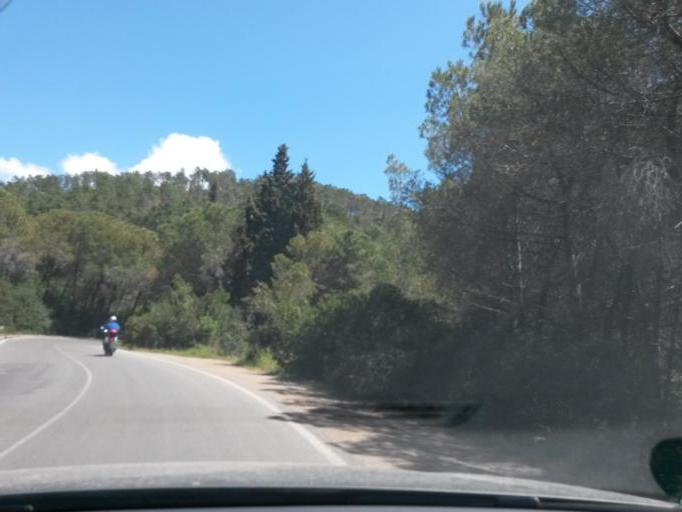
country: IT
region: Tuscany
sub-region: Provincia di Livorno
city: Portoferraio
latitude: 42.7644
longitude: 10.3276
